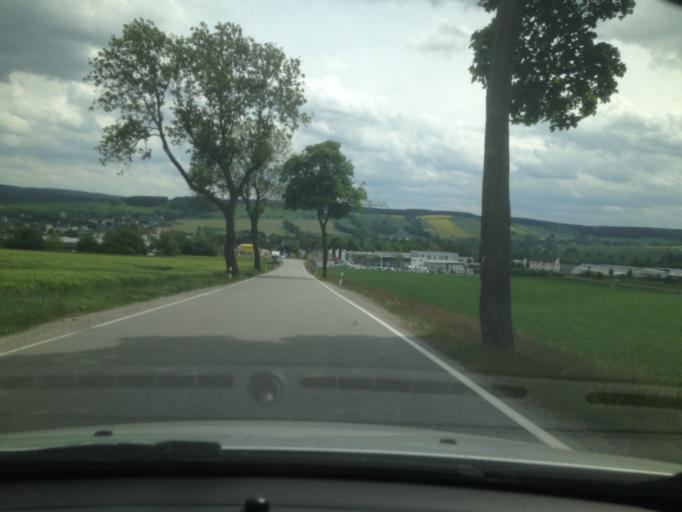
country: DE
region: Saxony
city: Zwonitz
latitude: 50.6376
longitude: 12.7911
